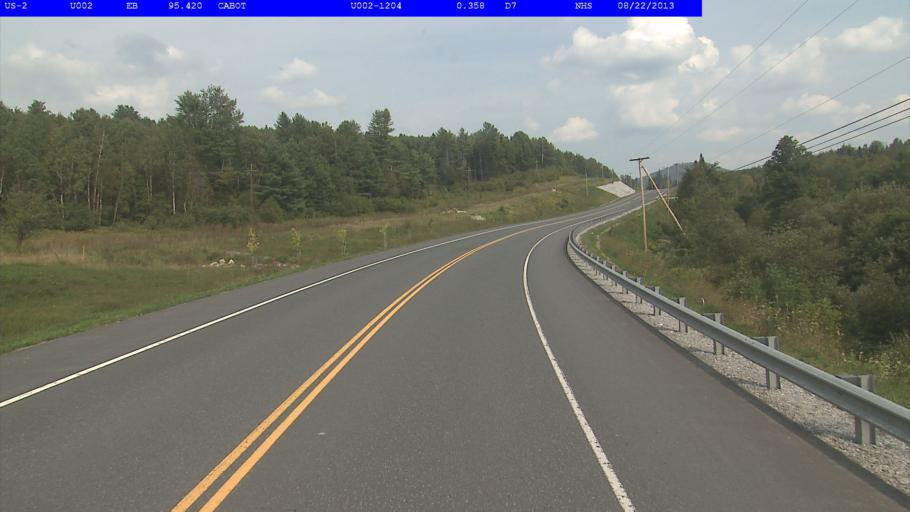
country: US
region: Vermont
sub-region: Caledonia County
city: Hardwick
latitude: 44.3638
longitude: -72.3174
